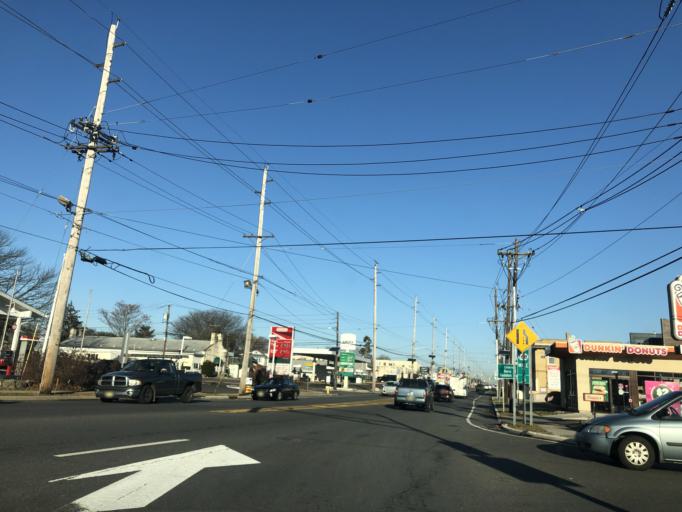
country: US
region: New Jersey
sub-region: Camden County
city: Mount Ephraim
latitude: 39.8735
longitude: -75.0825
